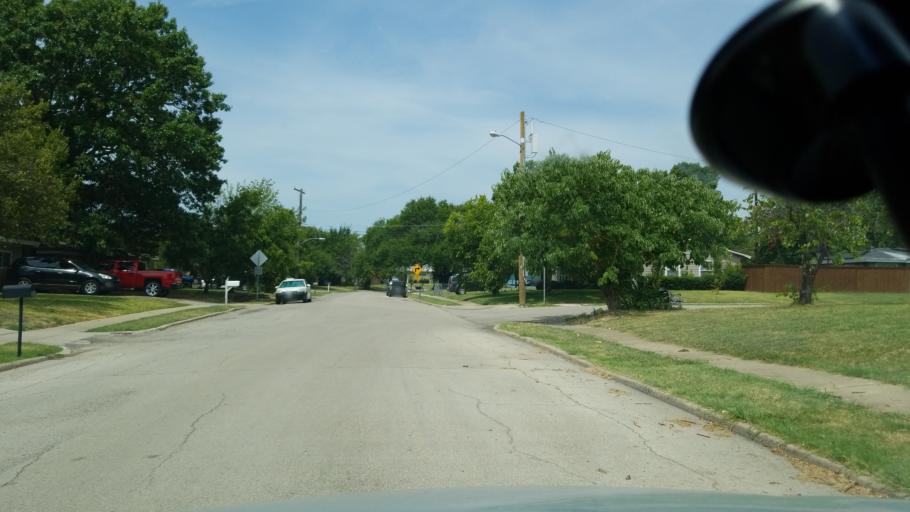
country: US
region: Texas
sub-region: Dallas County
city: Irving
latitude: 32.8295
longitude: -96.9861
